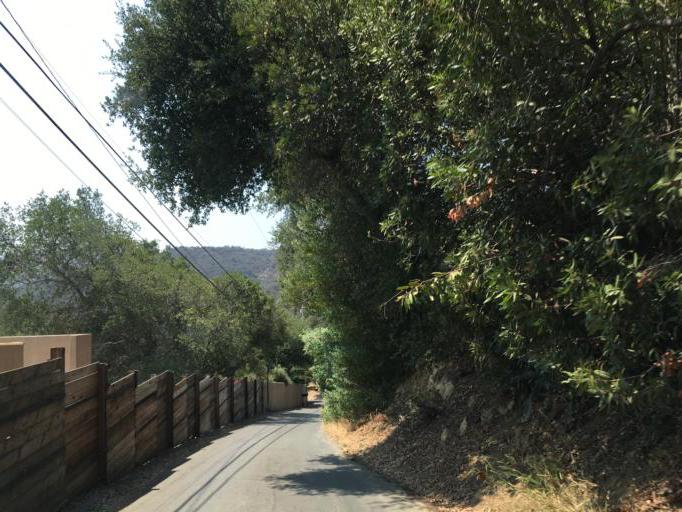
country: US
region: California
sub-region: Los Angeles County
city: Topanga
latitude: 34.1039
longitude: -118.5902
